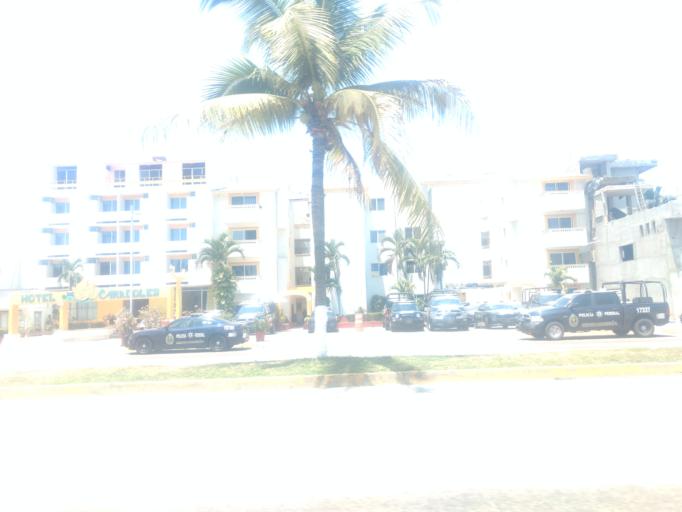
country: MX
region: Colima
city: Tapeixtles
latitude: 19.0898
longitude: -104.3131
